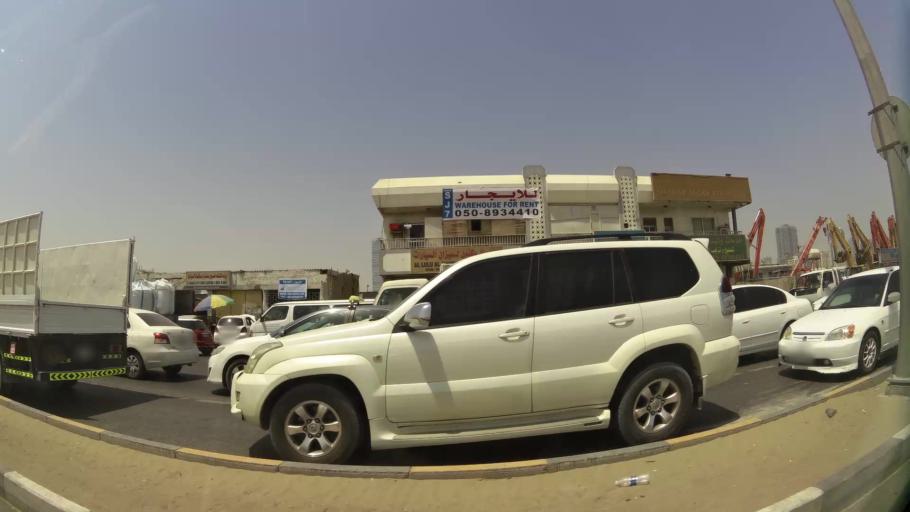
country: AE
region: Ash Shariqah
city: Sharjah
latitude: 25.3089
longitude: 55.3895
